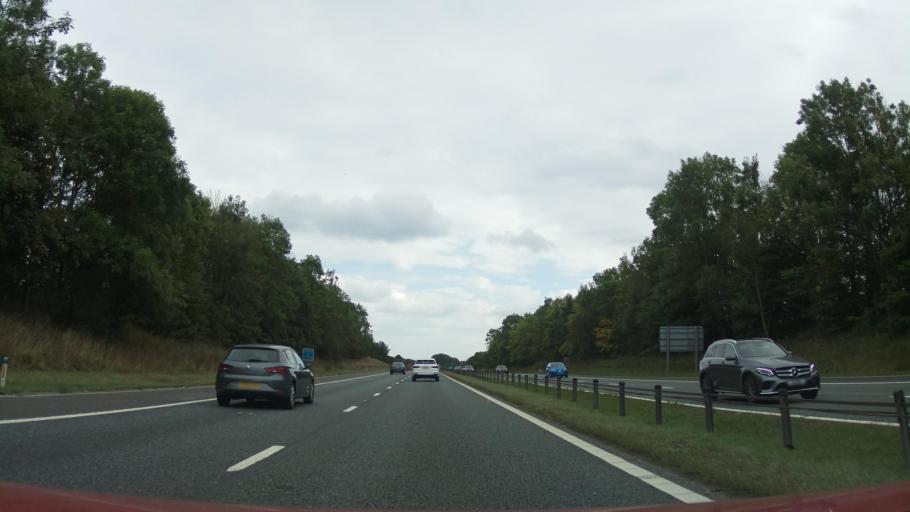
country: GB
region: England
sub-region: County Durham
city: Chester-le-Street
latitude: 54.8563
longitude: -1.5483
